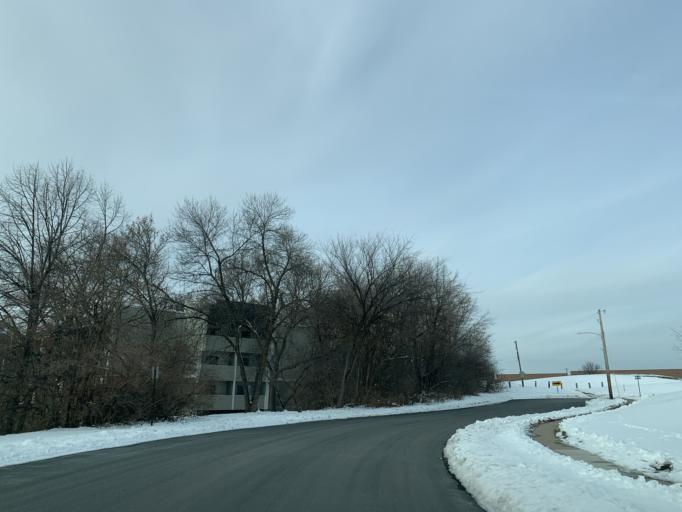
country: US
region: Minnesota
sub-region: Scott County
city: Savage
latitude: 44.8222
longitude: -93.3476
